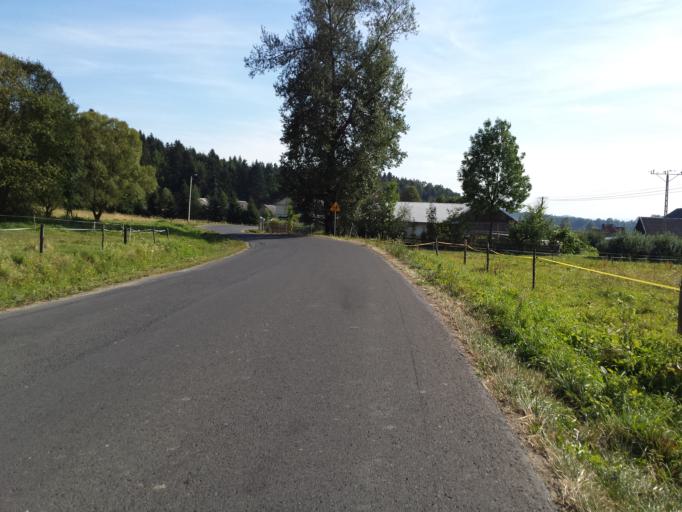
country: PL
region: Subcarpathian Voivodeship
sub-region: Powiat leski
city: Olszanica
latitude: 49.4951
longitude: 22.4498
